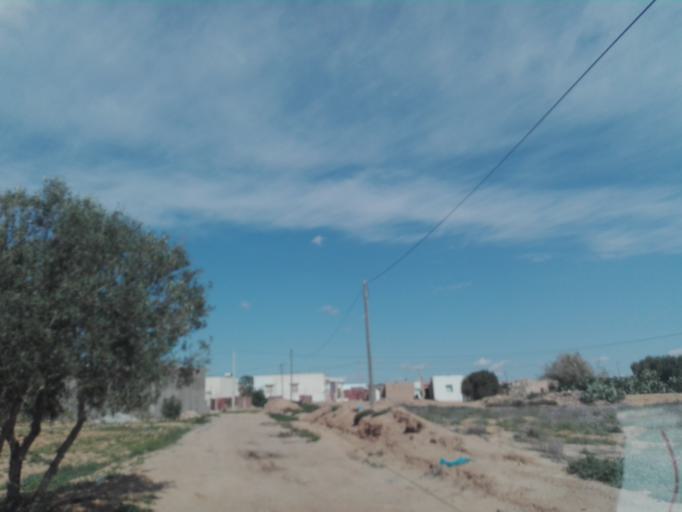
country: TN
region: Safaqis
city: Sfax
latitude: 34.7315
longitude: 10.5084
